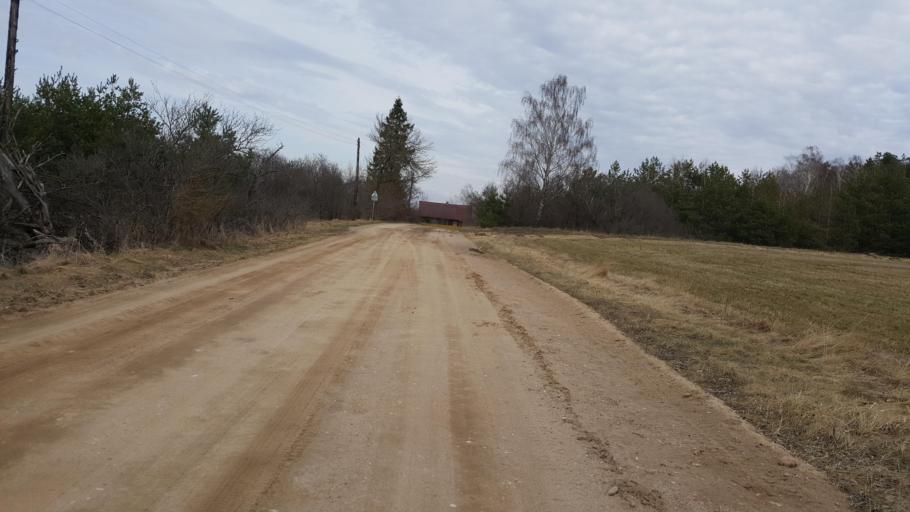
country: BY
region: Brest
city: Kamyanyets
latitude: 52.3725
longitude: 23.9810
